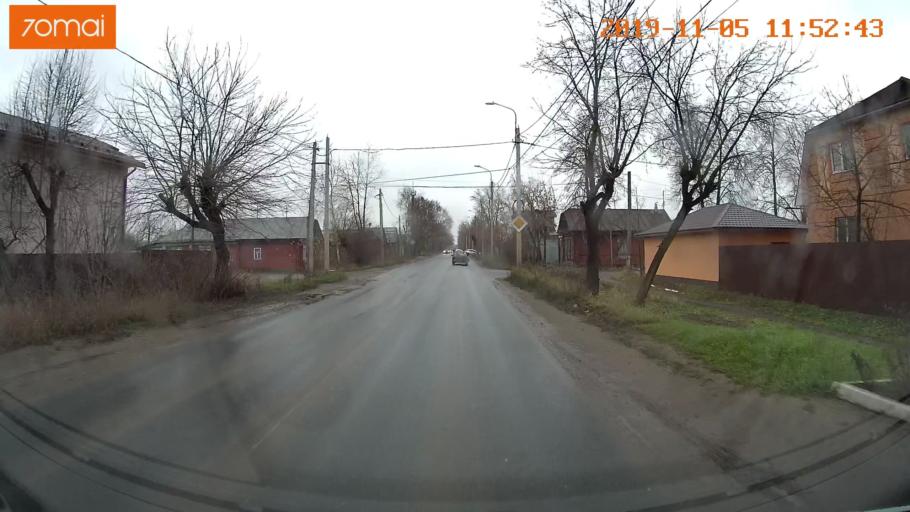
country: RU
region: Ivanovo
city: Bogorodskoye
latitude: 56.9989
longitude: 41.0296
